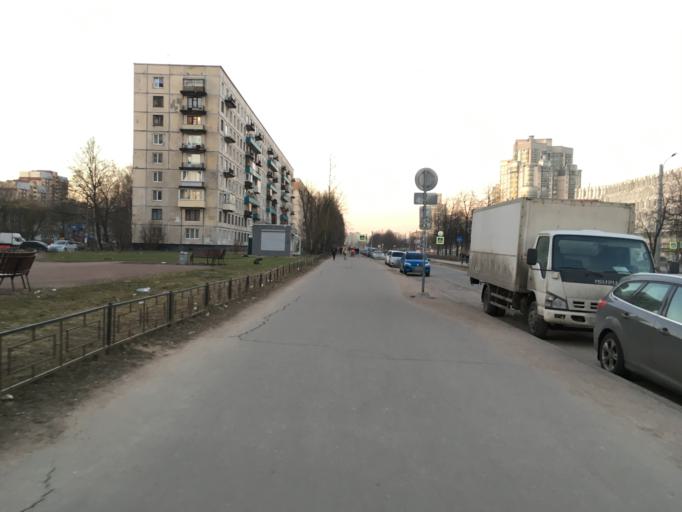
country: RU
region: St.-Petersburg
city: Grazhdanka
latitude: 60.0287
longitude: 30.4125
